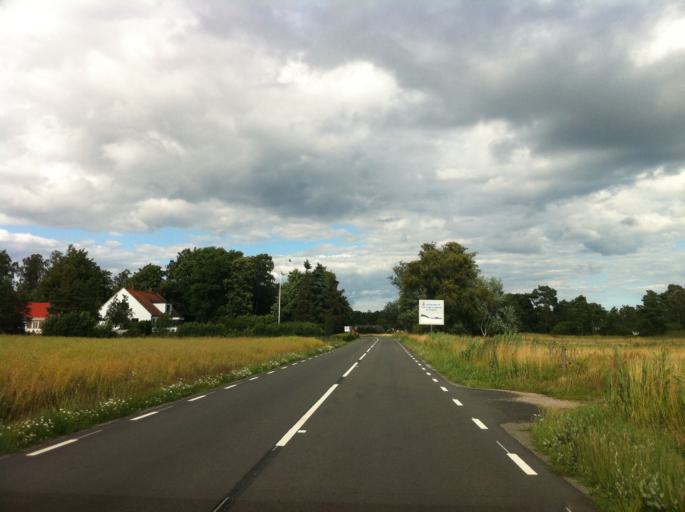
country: SE
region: Skane
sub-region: Simrishamns Kommun
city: Simrishamn
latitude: 55.4005
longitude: 14.1826
